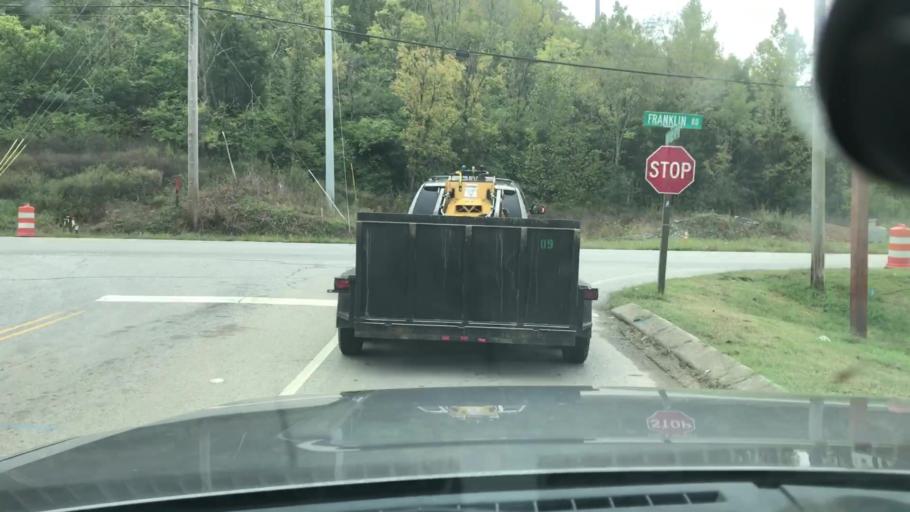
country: US
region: Tennessee
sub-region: Williamson County
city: Franklin
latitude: 35.9763
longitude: -86.8293
